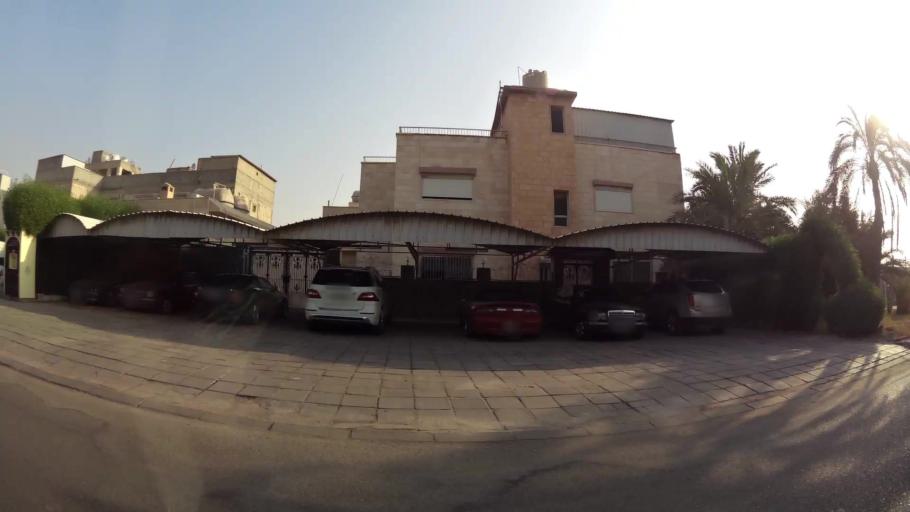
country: KW
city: Bayan
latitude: 29.2997
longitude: 48.0497
